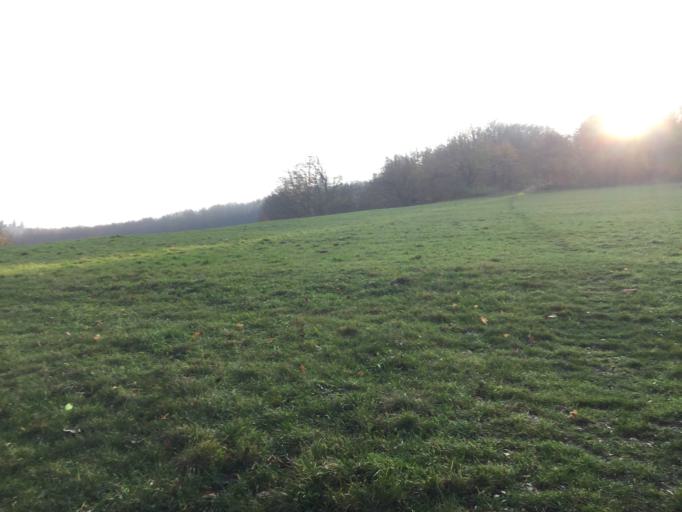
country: AT
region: Lower Austria
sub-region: Politischer Bezirk Wien-Umgebung
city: Gablitz
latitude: 48.2175
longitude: 16.1536
